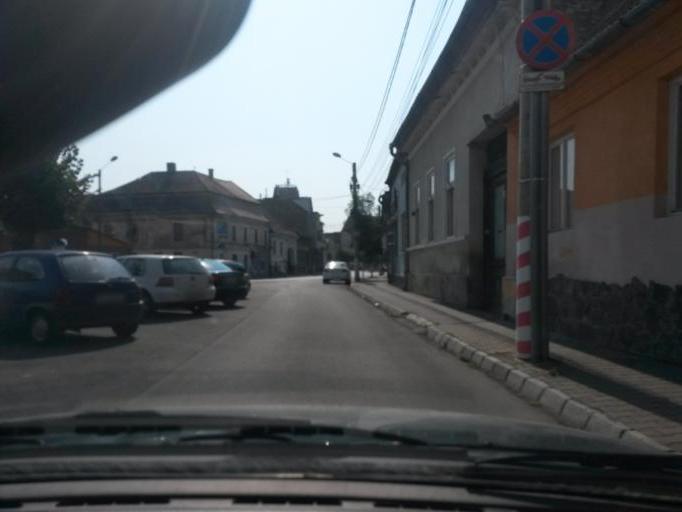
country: RO
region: Mures
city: Targu-Mures
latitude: 46.5482
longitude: 24.5580
